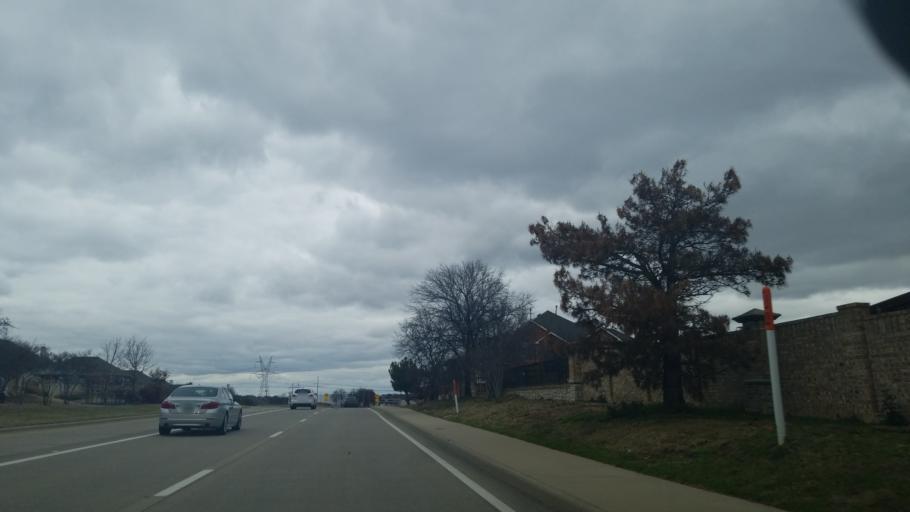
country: US
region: Texas
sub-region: Denton County
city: Copper Canyon
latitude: 33.0839
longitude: -97.0779
